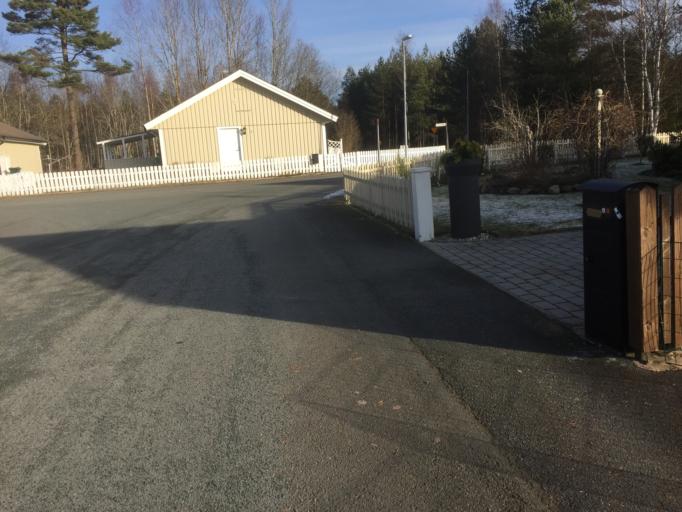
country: SE
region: Joenkoeping
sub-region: Aneby Kommun
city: Aneby
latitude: 57.8464
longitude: 14.7958
